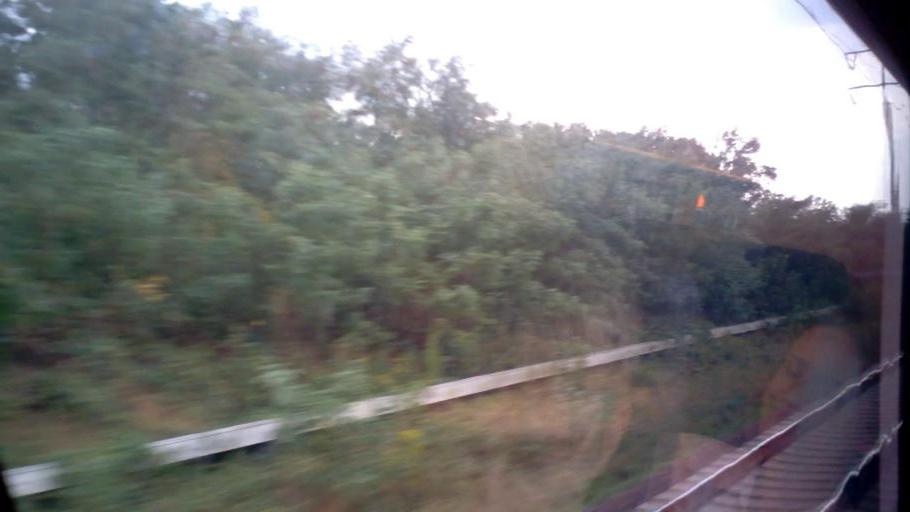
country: DE
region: Berlin
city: Lichtenrade
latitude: 52.3601
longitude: 13.4427
